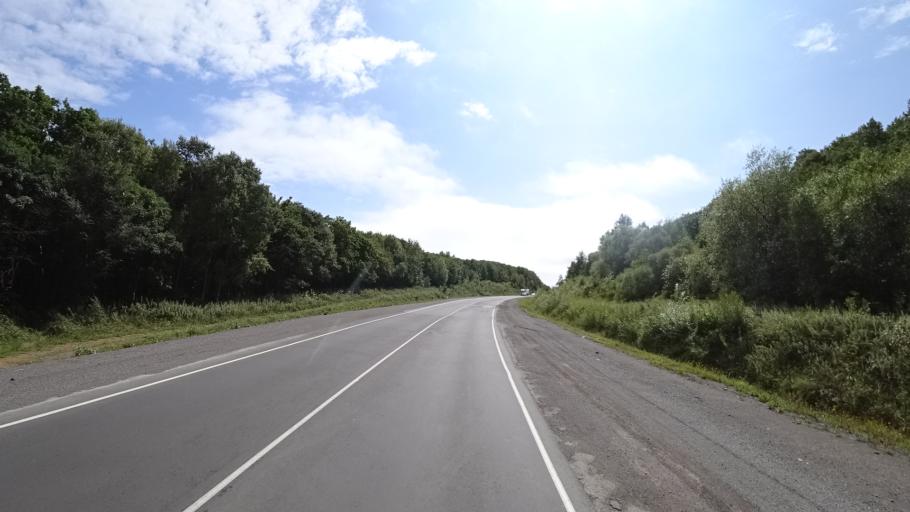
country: RU
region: Primorskiy
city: Lyalichi
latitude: 44.1317
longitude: 132.4273
